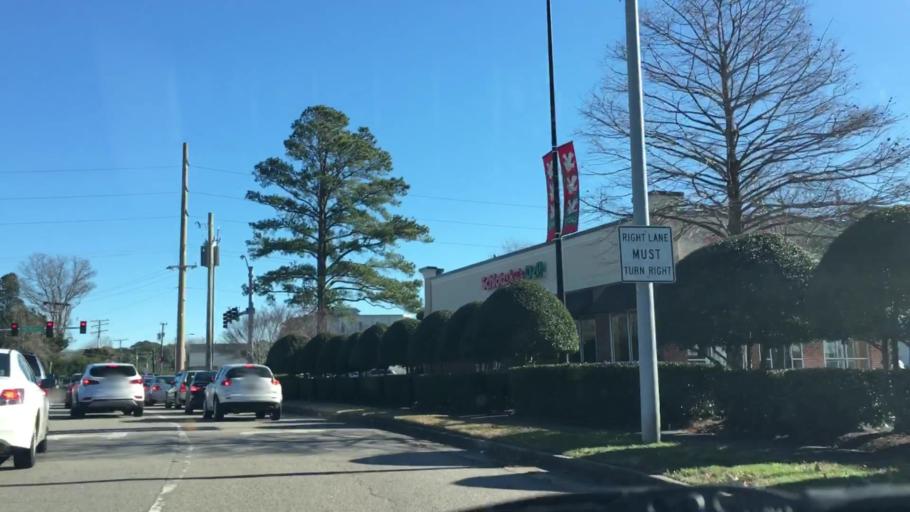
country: US
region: Virginia
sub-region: City of Virginia Beach
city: Virginia Beach
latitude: 36.8529
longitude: -76.0236
